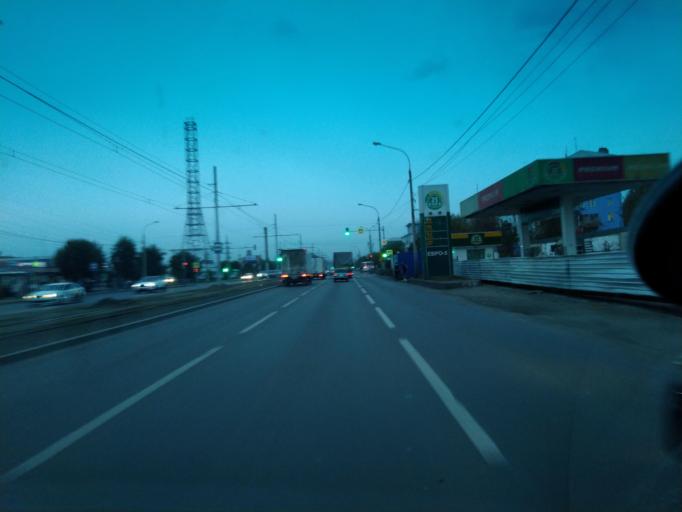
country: RU
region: Krasnoyarskiy
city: Berezovka
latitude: 56.0225
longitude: 93.0127
